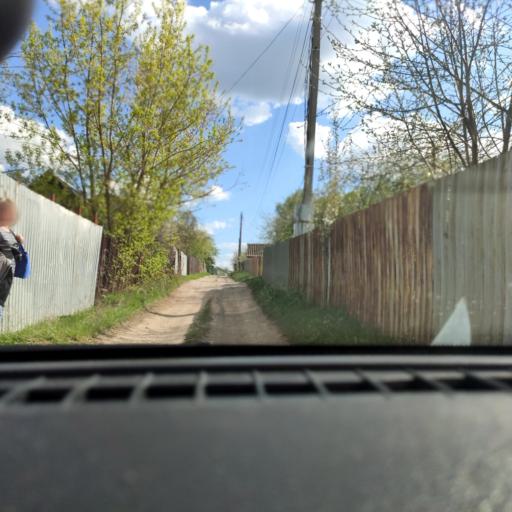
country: RU
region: Samara
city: Zhigulevsk
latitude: 53.3720
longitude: 49.5093
